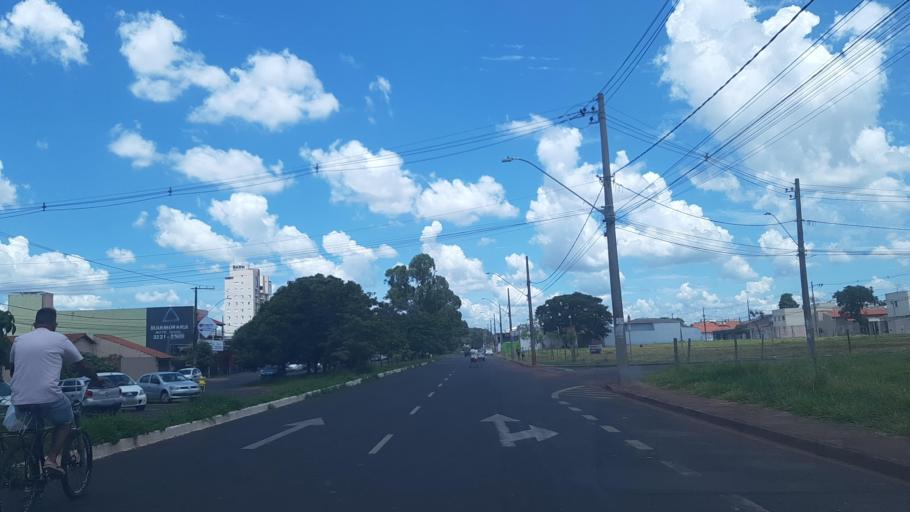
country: BR
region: Minas Gerais
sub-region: Uberlandia
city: Uberlandia
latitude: -18.9504
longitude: -48.3221
